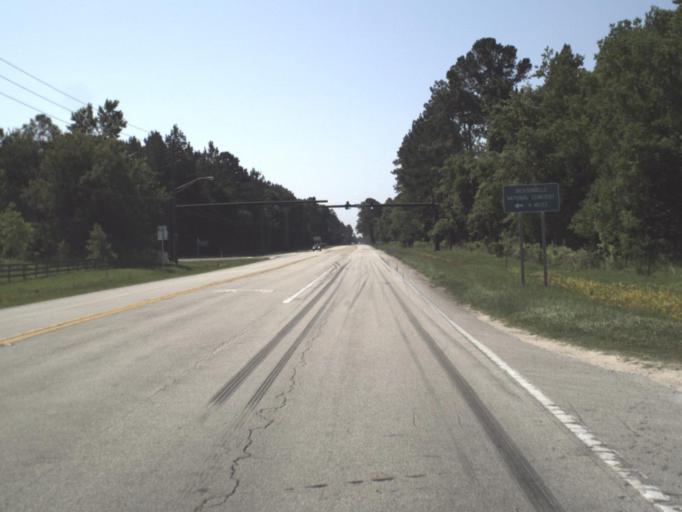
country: US
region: Florida
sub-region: Nassau County
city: Nassau Village-Ratliff
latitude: 30.5093
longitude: -81.7560
